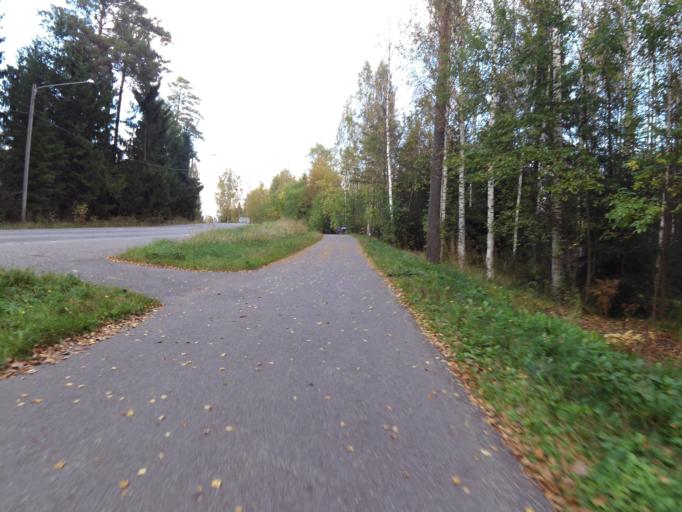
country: FI
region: Uusimaa
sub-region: Helsinki
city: Kauniainen
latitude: 60.2984
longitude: 24.7357
